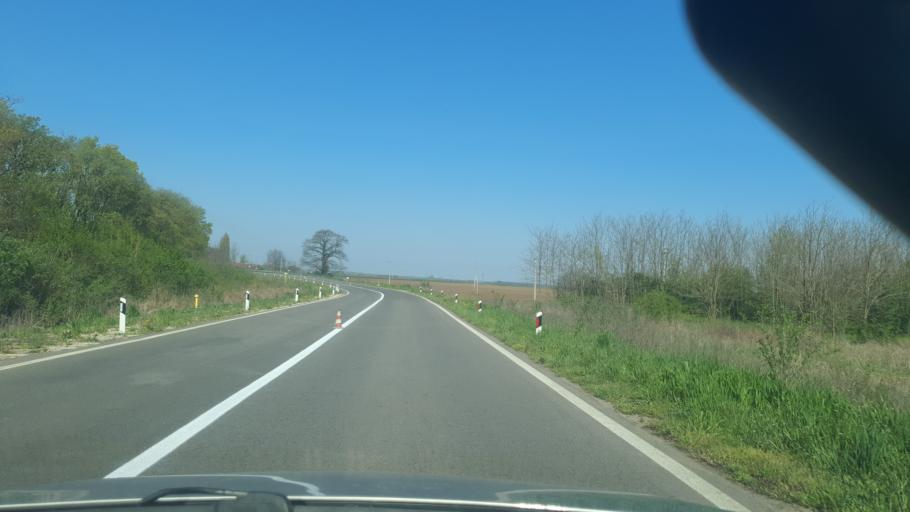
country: RS
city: Gakovo
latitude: 45.8374
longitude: 19.0077
